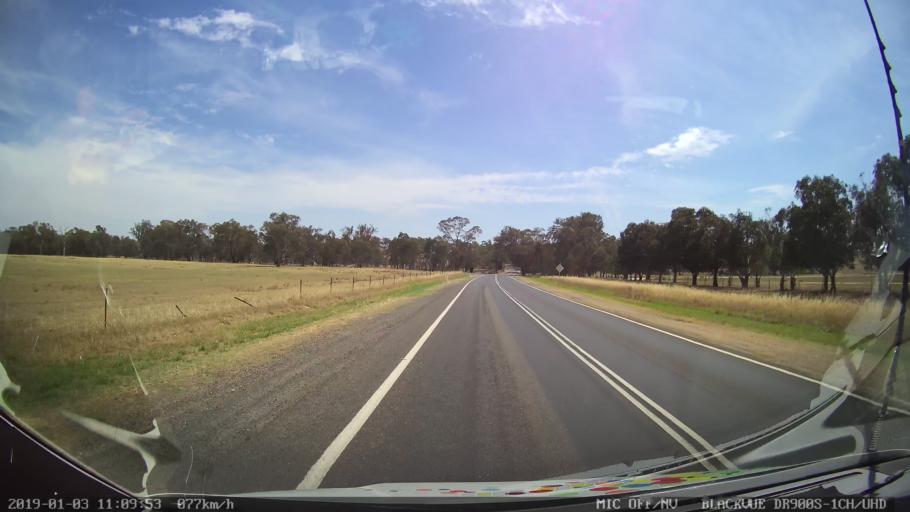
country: AU
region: New South Wales
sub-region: Young
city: Young
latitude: -34.2330
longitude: 148.2563
